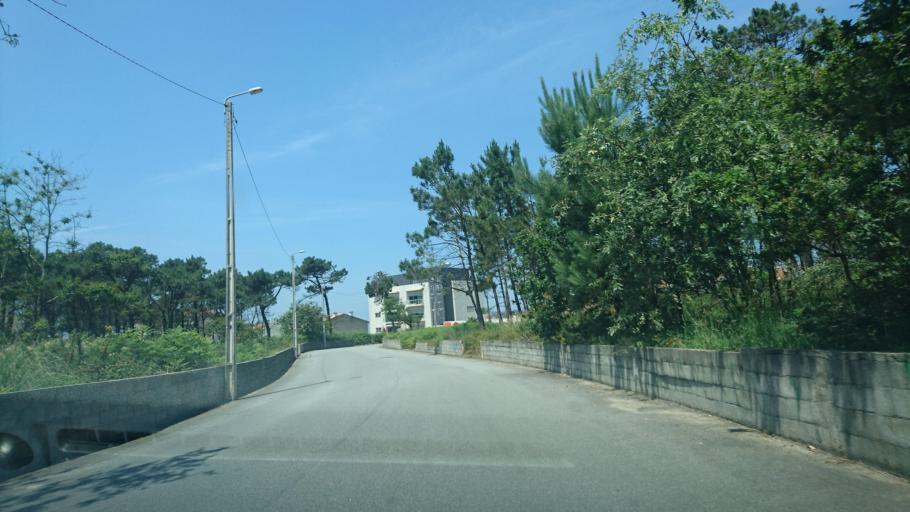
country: PT
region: Porto
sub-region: Matosinhos
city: Lavra
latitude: 41.2715
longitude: -8.7221
